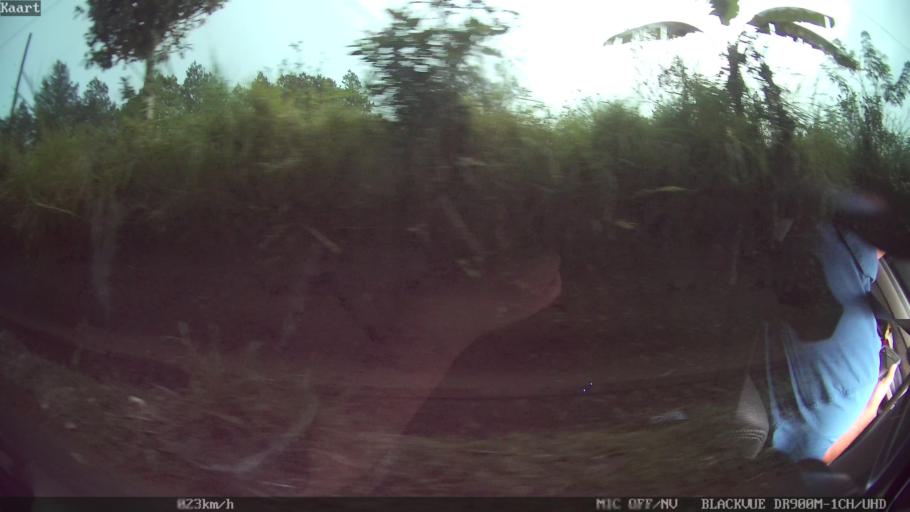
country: ID
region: Bali
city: Banjar Kedisan
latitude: -8.2651
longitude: 115.3323
